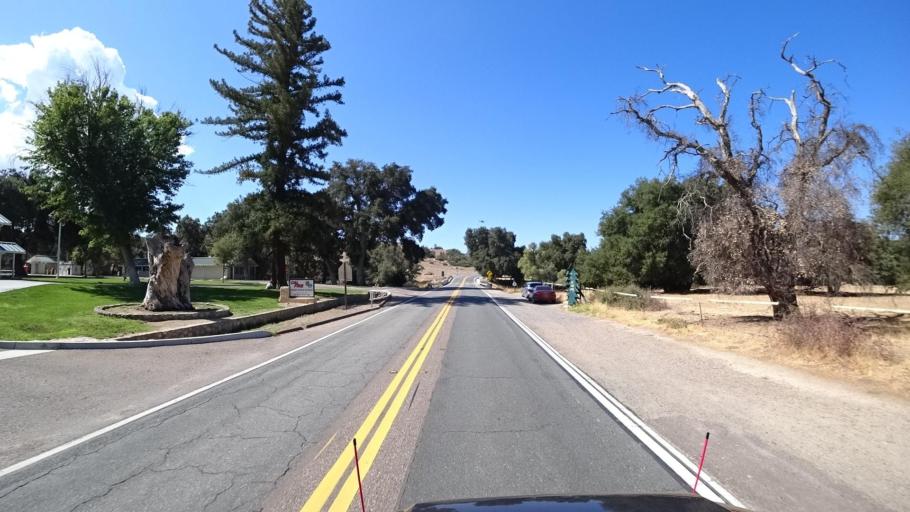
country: US
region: California
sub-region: San Diego County
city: Julian
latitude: 33.2739
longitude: -116.6445
